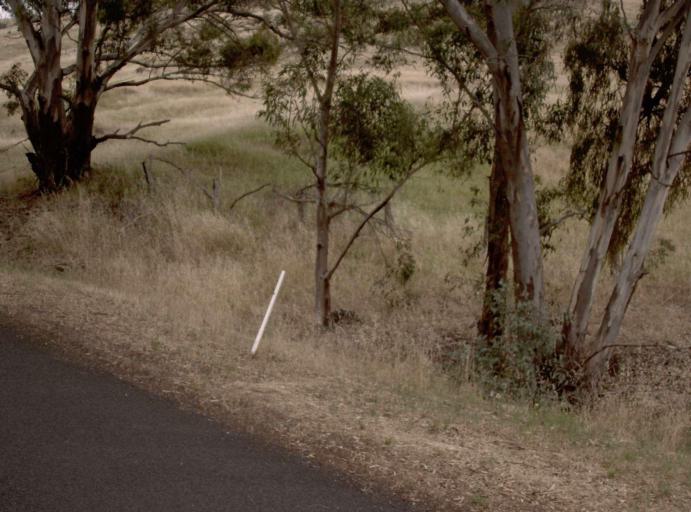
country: AU
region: Victoria
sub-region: Wellington
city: Heyfield
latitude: -37.6838
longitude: 146.6570
